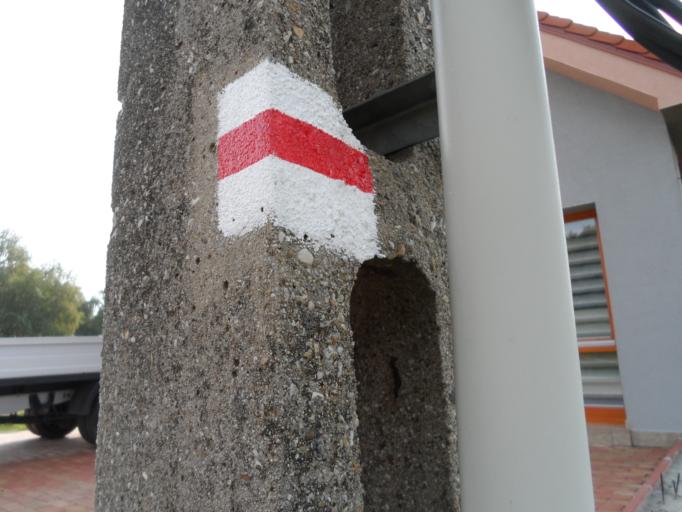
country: HU
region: Veszprem
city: Zirc
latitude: 47.3100
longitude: 17.9228
